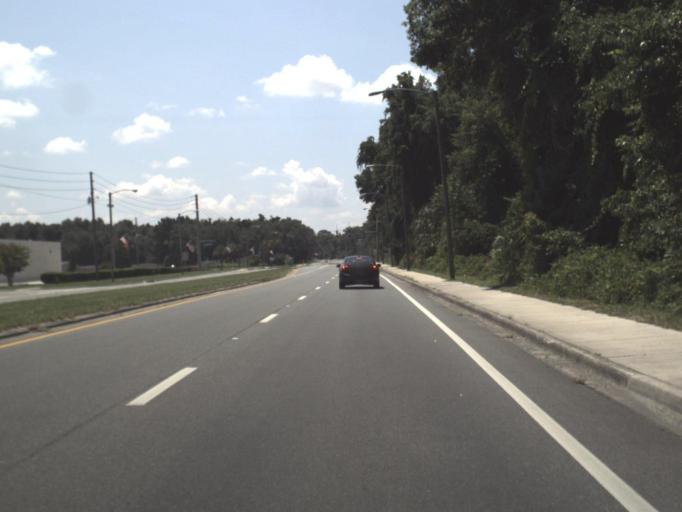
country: US
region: Florida
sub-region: Citrus County
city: Crystal River
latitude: 28.9087
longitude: -82.6050
